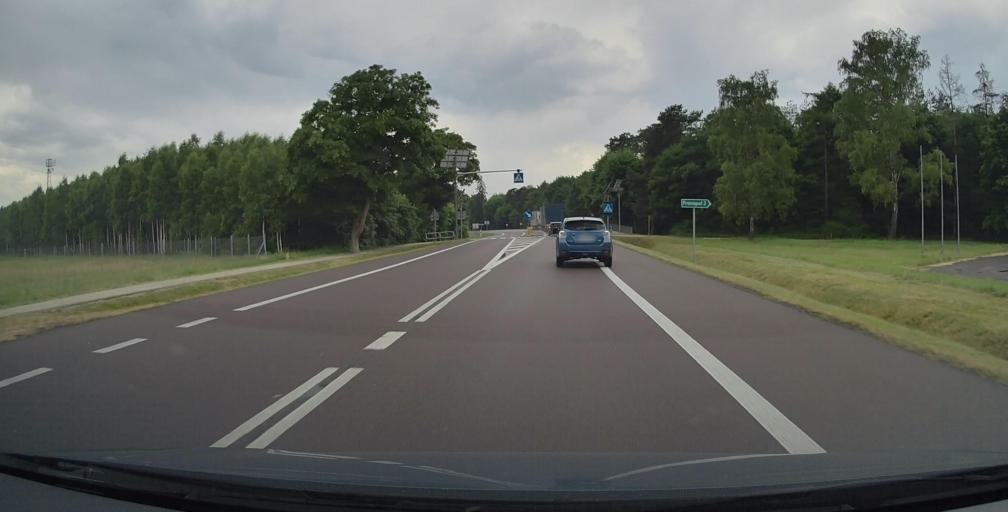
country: PL
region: Lublin Voivodeship
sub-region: Powiat bialski
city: Lesna Podlaska
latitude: 52.0386
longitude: 22.9479
